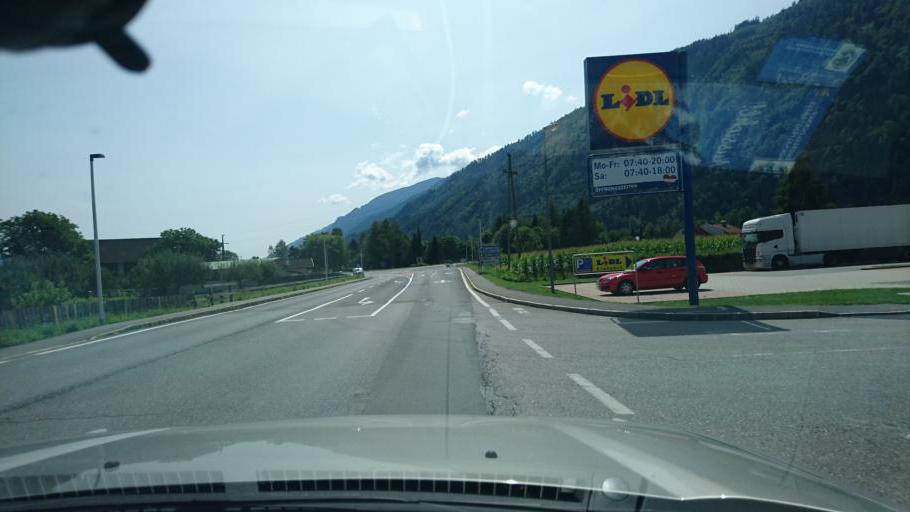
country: AT
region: Carinthia
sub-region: Politischer Bezirk Spittal an der Drau
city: Sachsenburg
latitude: 46.8333
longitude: 13.3788
